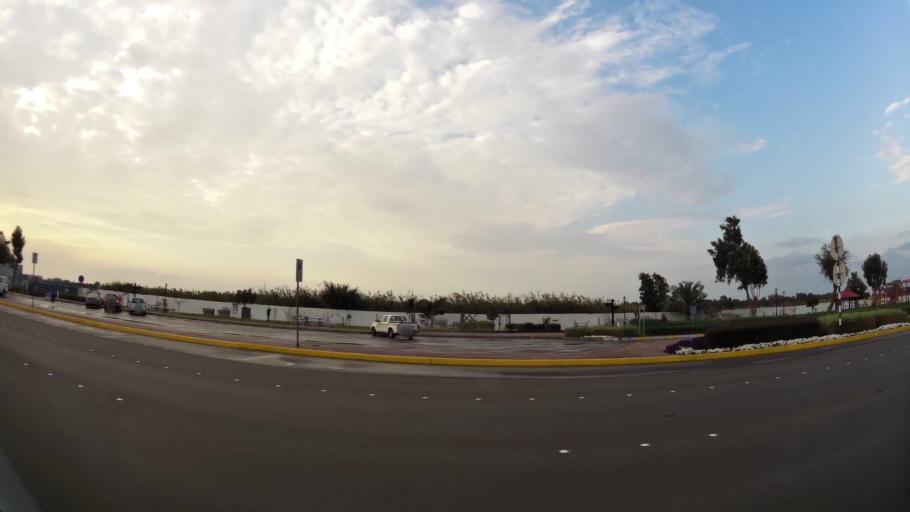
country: AE
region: Abu Dhabi
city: Abu Dhabi
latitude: 24.4199
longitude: 54.4262
